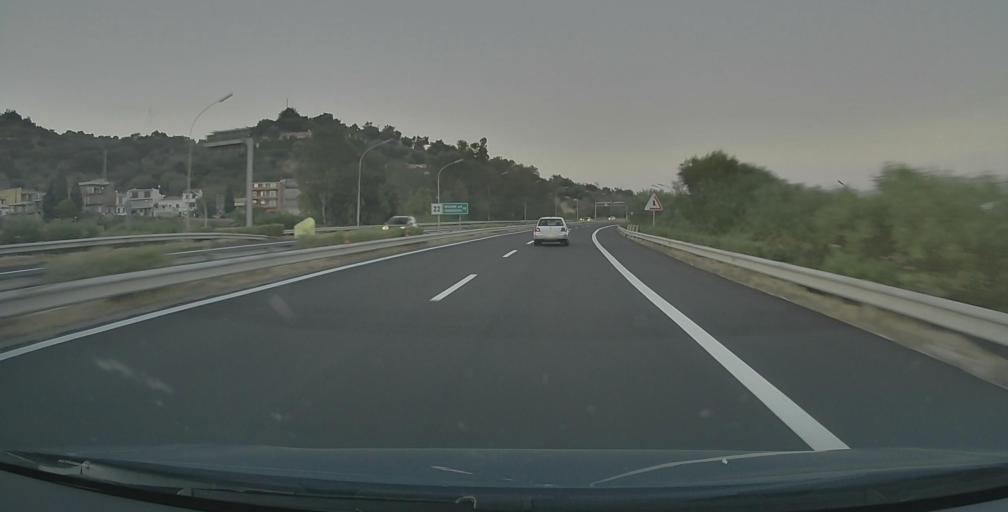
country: IT
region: Sicily
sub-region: Messina
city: Furci Siculo
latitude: 37.9695
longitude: 15.3845
